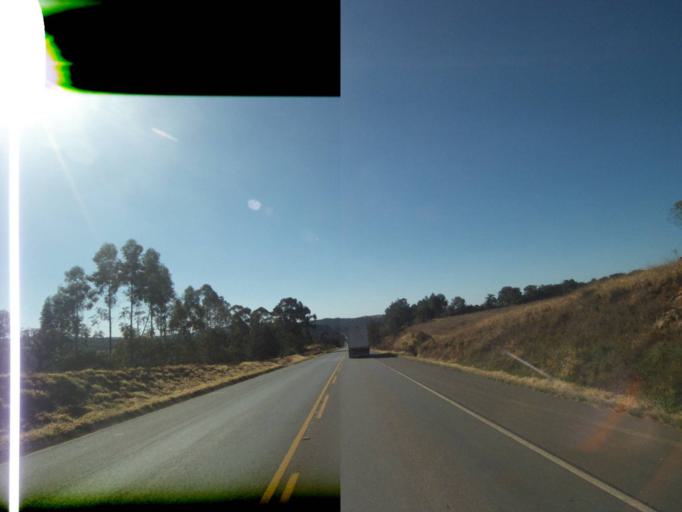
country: BR
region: Parana
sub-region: Tibagi
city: Tibagi
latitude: -24.5971
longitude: -50.4376
